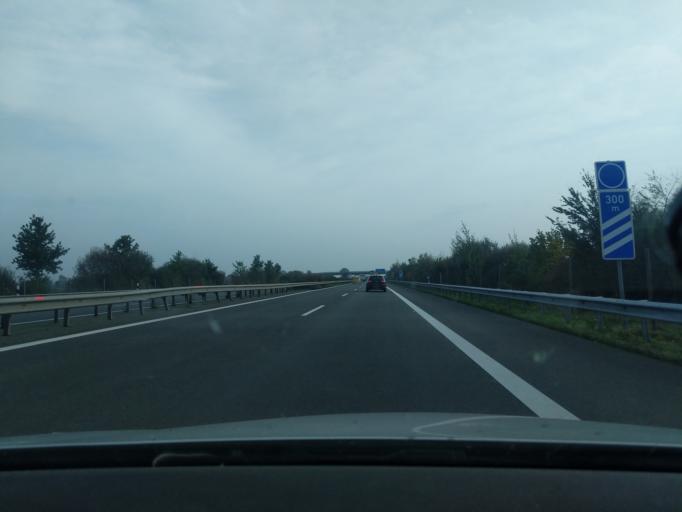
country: DE
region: Lower Saxony
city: Dollern
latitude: 53.5483
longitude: 9.5661
